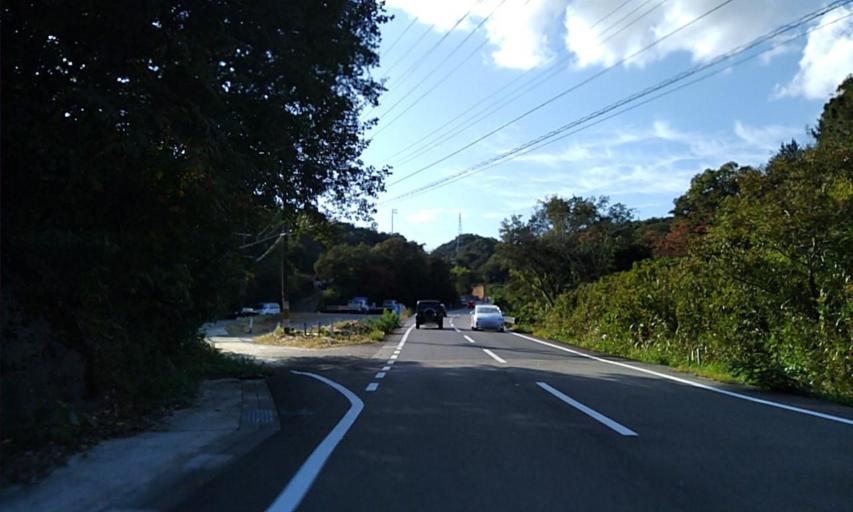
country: JP
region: Wakayama
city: Tanabe
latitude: 33.6827
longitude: 135.4021
